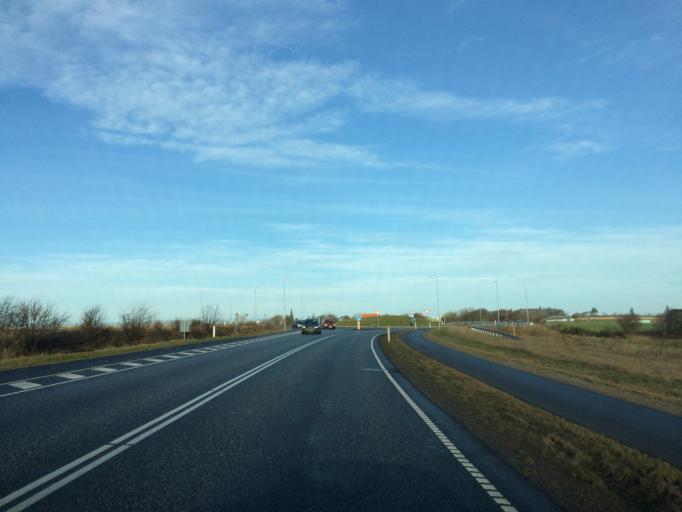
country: DK
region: Central Jutland
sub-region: Struer Kommune
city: Struer
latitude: 56.5115
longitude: 8.5686
